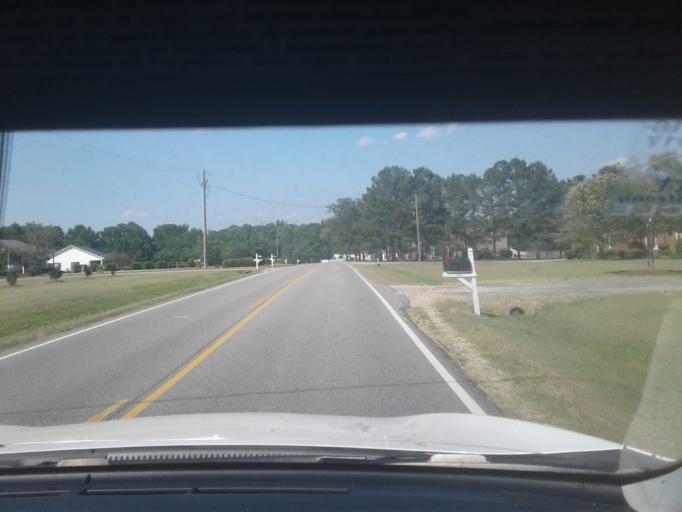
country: US
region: North Carolina
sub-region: Johnston County
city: Benson
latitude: 35.3944
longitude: -78.6042
